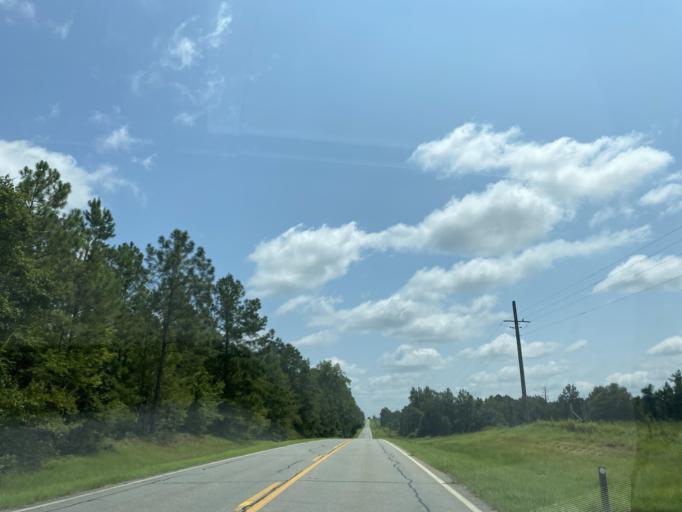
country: US
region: Georgia
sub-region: Wilcox County
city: Abbeville
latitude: 32.0096
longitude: -83.1128
